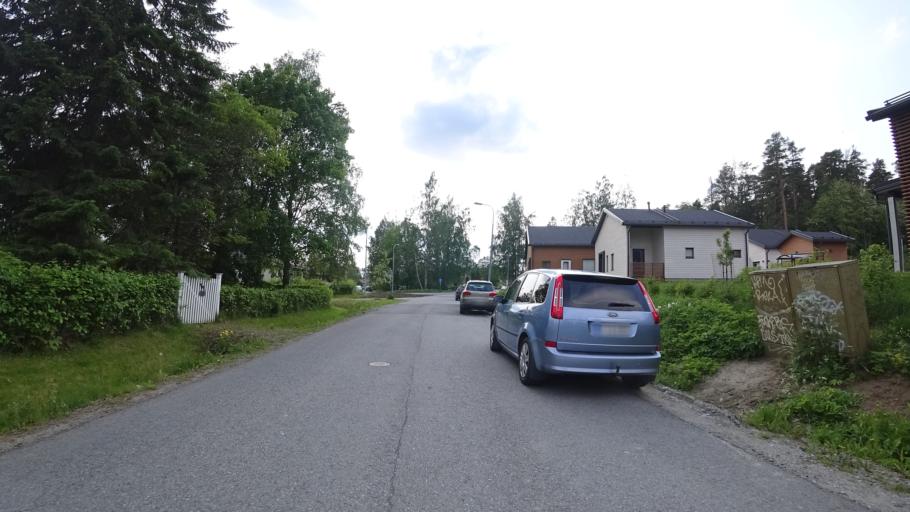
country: FI
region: Pirkanmaa
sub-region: Tampere
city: Pirkkala
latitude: 61.4984
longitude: 23.6461
